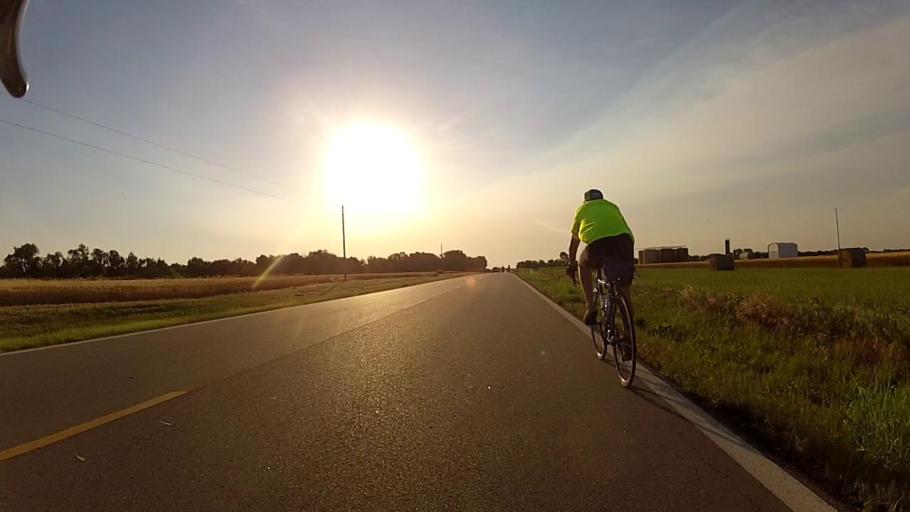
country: US
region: Kansas
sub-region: Harper County
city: Anthony
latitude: 37.1540
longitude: -97.8426
